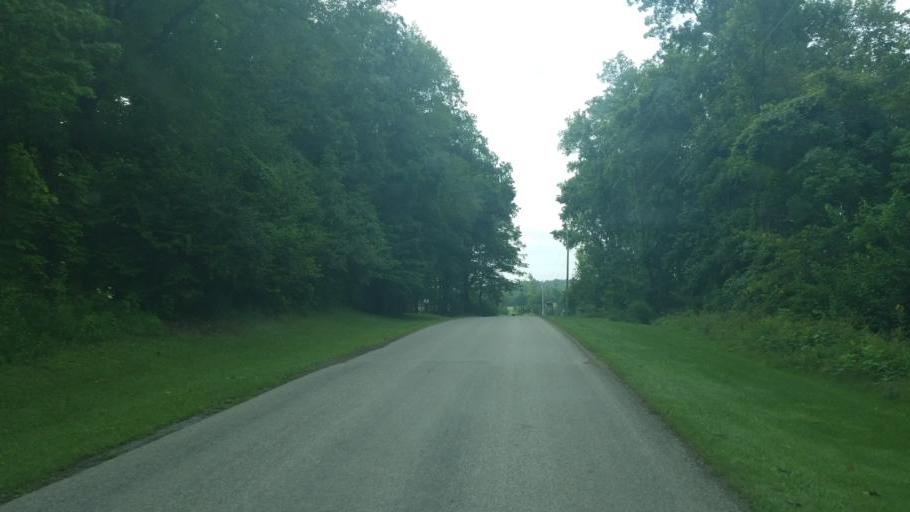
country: US
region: Ohio
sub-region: Knox County
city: Fredericktown
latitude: 40.4577
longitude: -82.6784
